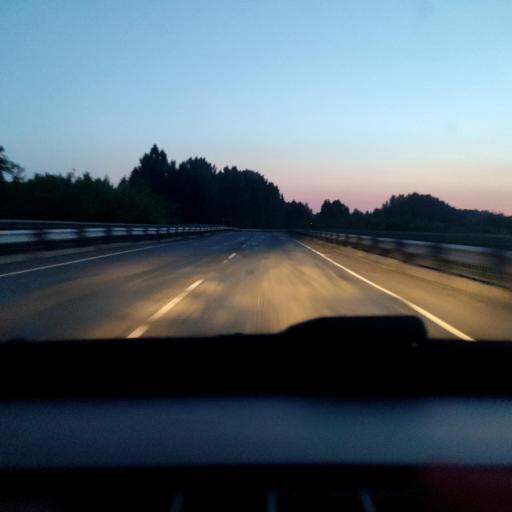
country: RU
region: Voronezj
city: Pridonskoy
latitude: 51.7833
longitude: 39.0532
